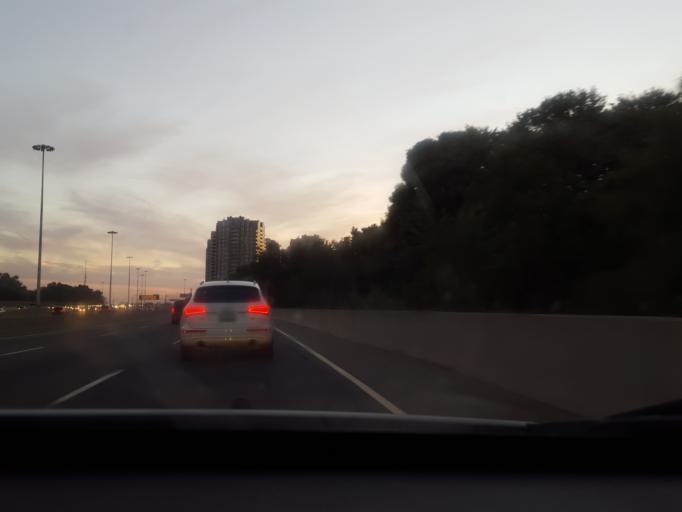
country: CA
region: Ontario
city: Willowdale
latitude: 43.7606
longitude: -79.3975
